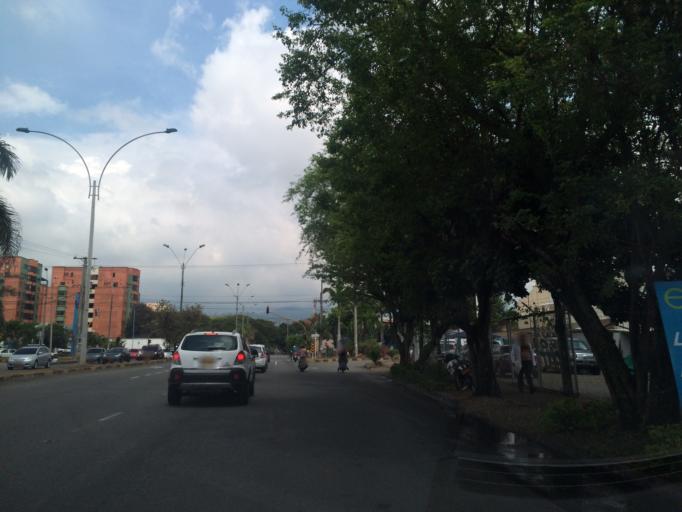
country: CO
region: Valle del Cauca
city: Cali
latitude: 3.3930
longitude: -76.5316
